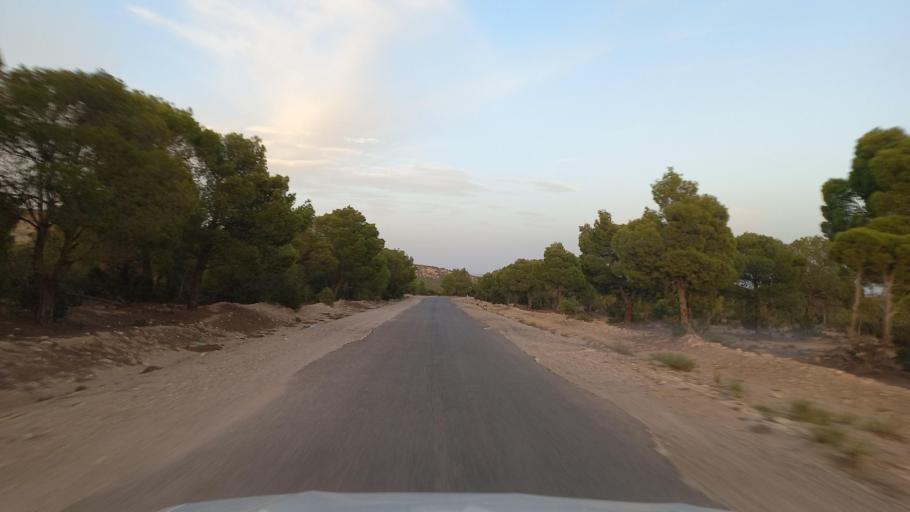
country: TN
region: Al Qasrayn
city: Sbiba
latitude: 35.4131
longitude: 8.9345
